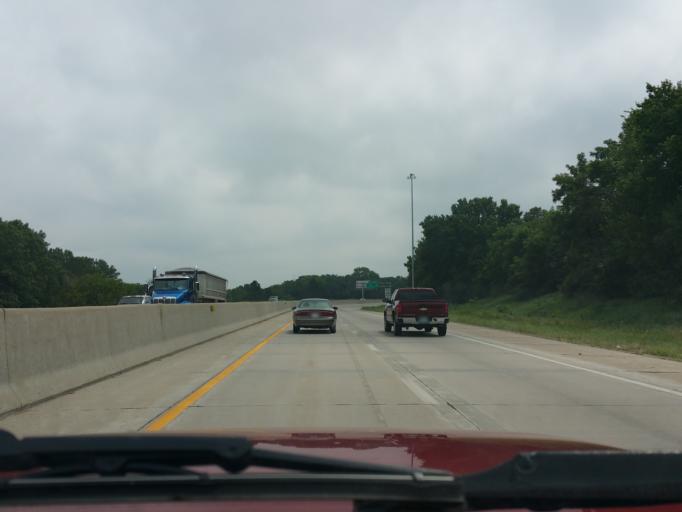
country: US
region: Kansas
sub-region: Shawnee County
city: Topeka
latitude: 39.0648
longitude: -95.6853
